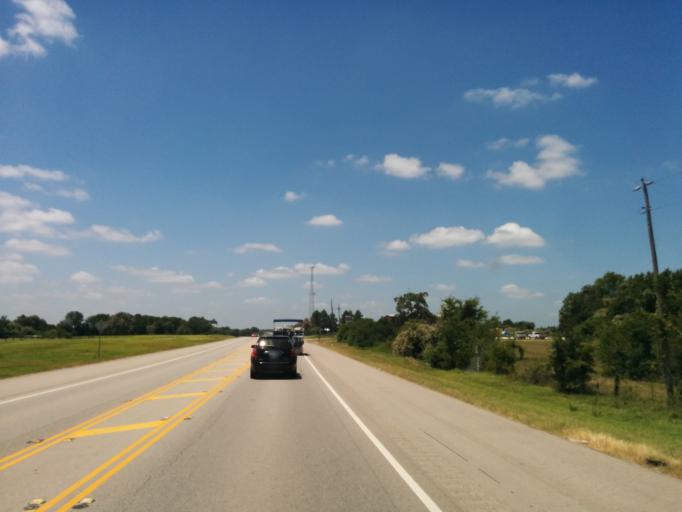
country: US
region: Texas
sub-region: Leon County
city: Hilltop Lakes
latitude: 30.8764
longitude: -96.1846
